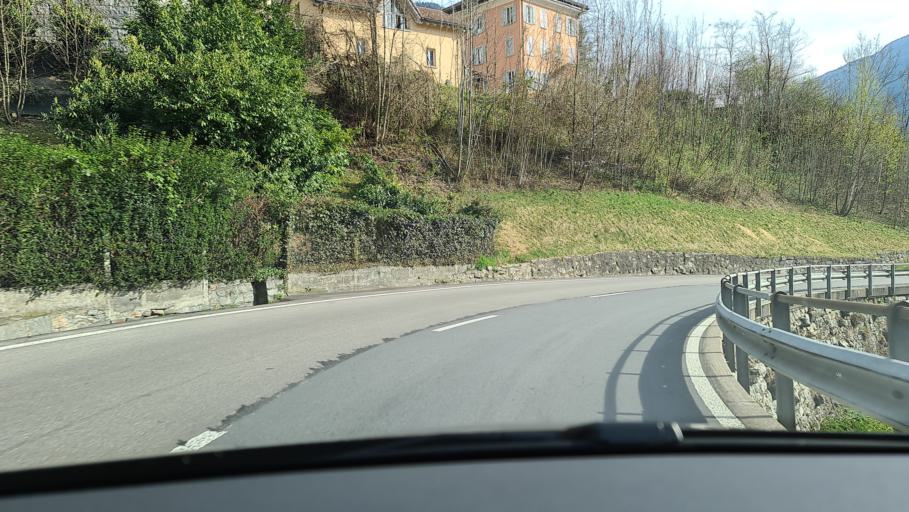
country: CH
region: Ticino
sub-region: Blenio District
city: Acquarossa
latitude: 46.4688
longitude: 8.9421
